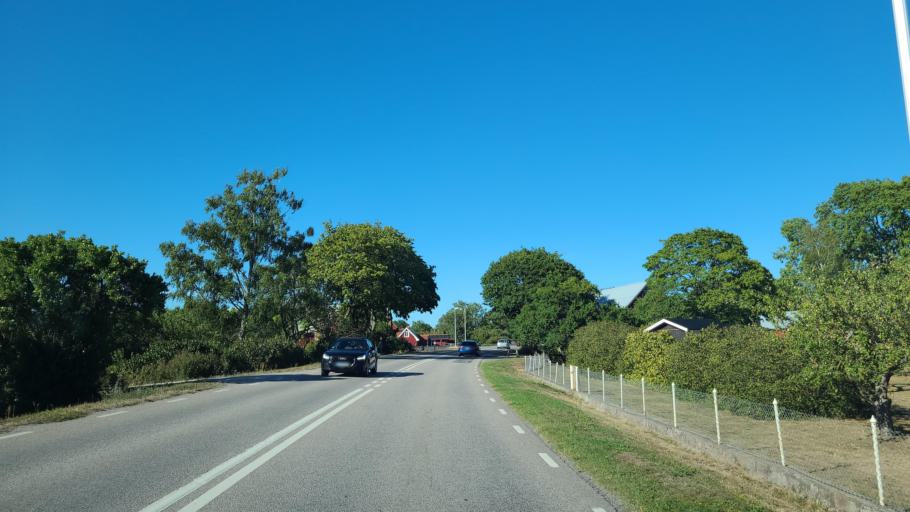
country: SE
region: Kalmar
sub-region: Borgholms Kommun
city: Borgholm
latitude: 57.2335
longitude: 17.0534
